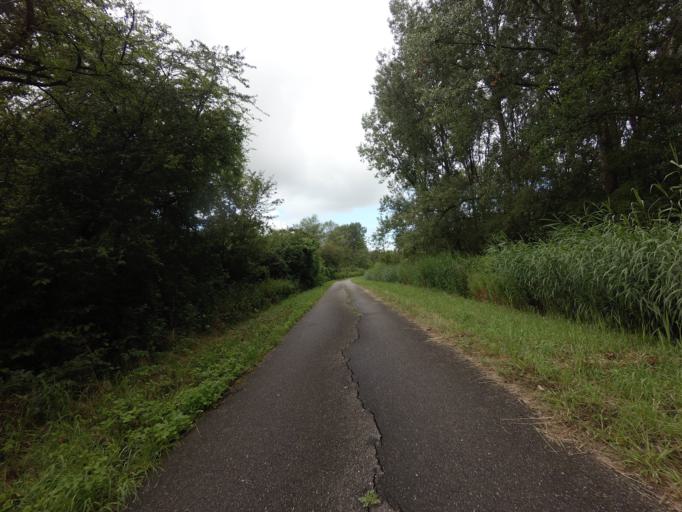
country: NL
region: North Holland
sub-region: Gemeente Velsen
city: Velsen-Zuid
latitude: 52.4377
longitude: 4.6950
